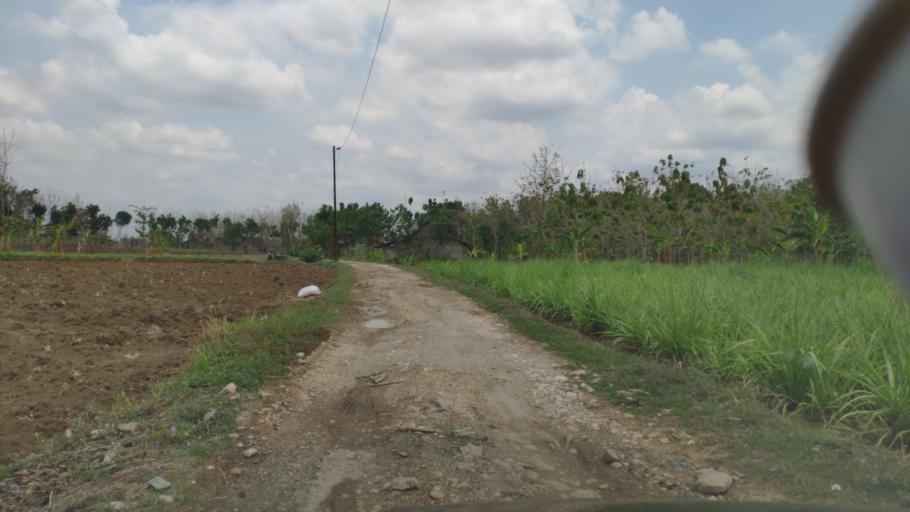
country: ID
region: Central Java
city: Gumiring
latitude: -7.0466
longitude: 111.3919
